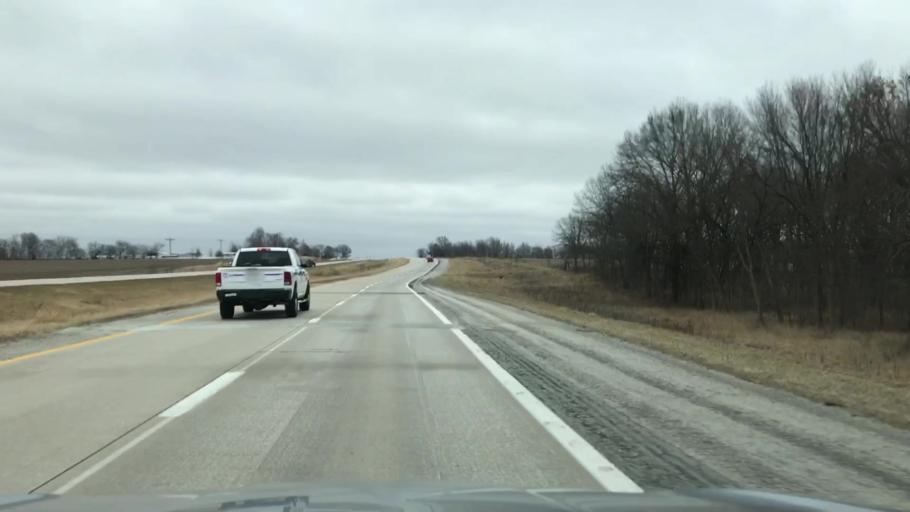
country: US
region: Missouri
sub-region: Livingston County
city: Chillicothe
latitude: 39.7772
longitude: -93.3597
